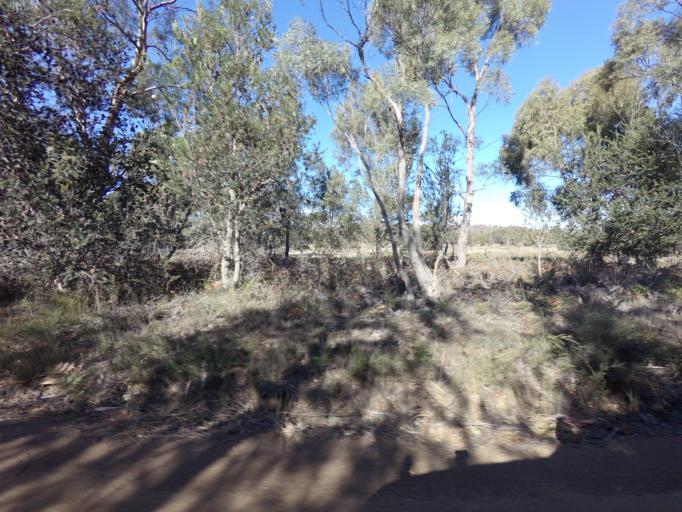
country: AU
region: Tasmania
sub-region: Sorell
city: Sorell
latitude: -42.3521
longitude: 147.9691
